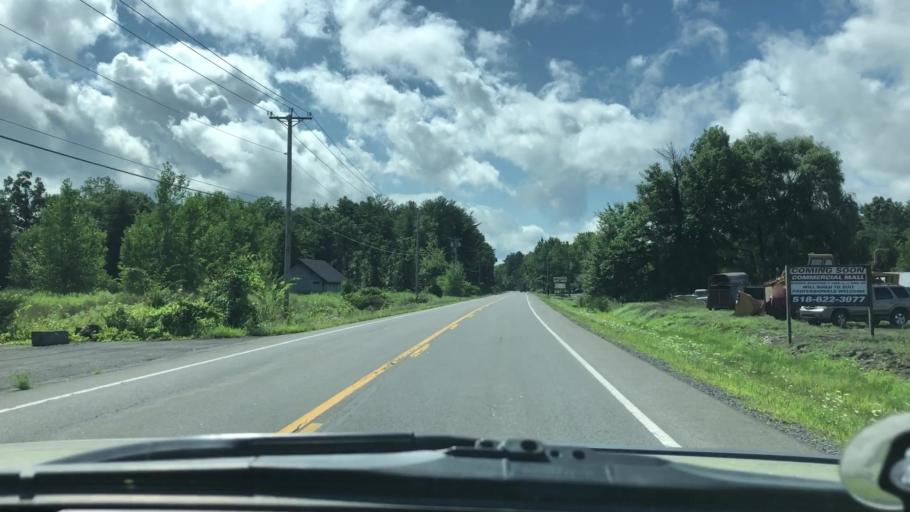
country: US
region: New York
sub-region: Greene County
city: Cairo
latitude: 42.2893
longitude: -73.9857
